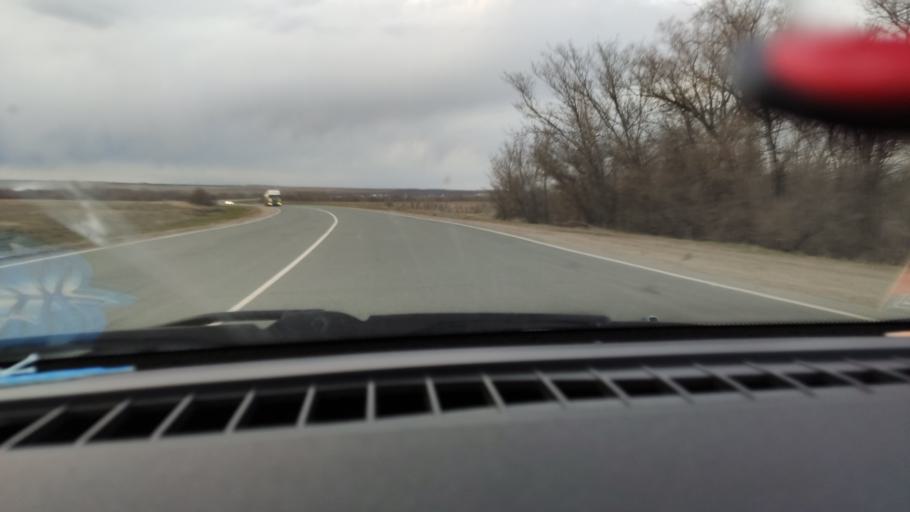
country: RU
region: Saratov
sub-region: Saratovskiy Rayon
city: Saratov
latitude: 51.7218
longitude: 46.0267
